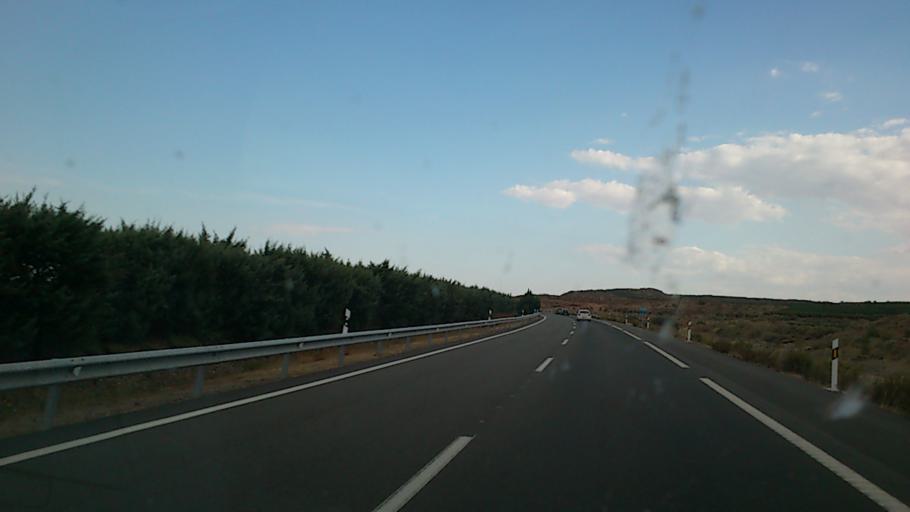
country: ES
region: La Rioja
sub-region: Provincia de La Rioja
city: Aldeanueva de Ebro
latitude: 42.2557
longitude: -1.9208
